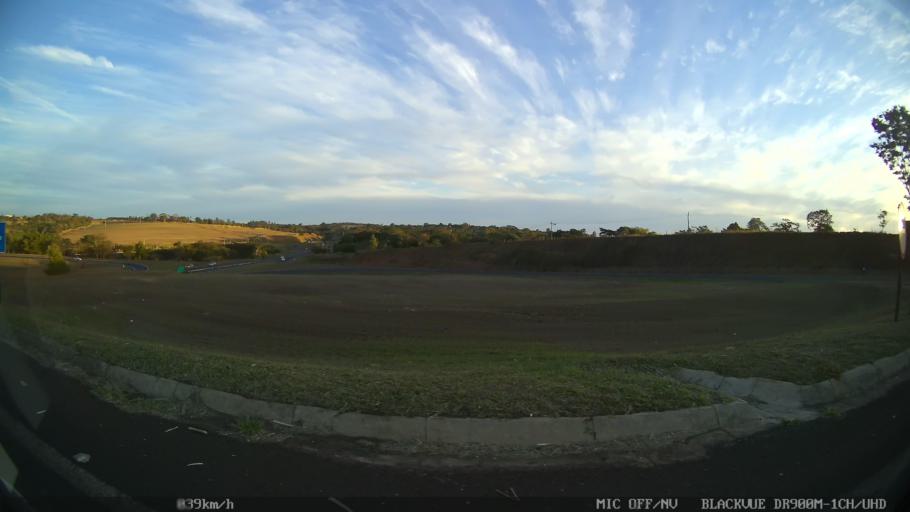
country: BR
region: Sao Paulo
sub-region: Catanduva
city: Catanduva
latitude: -21.1598
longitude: -48.9878
